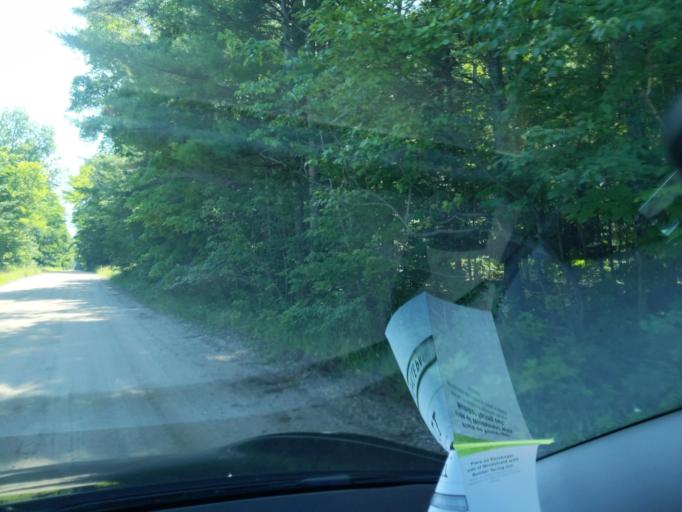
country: US
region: Michigan
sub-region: Cheboygan County
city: Cheboygan
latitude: 45.6791
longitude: -84.6566
